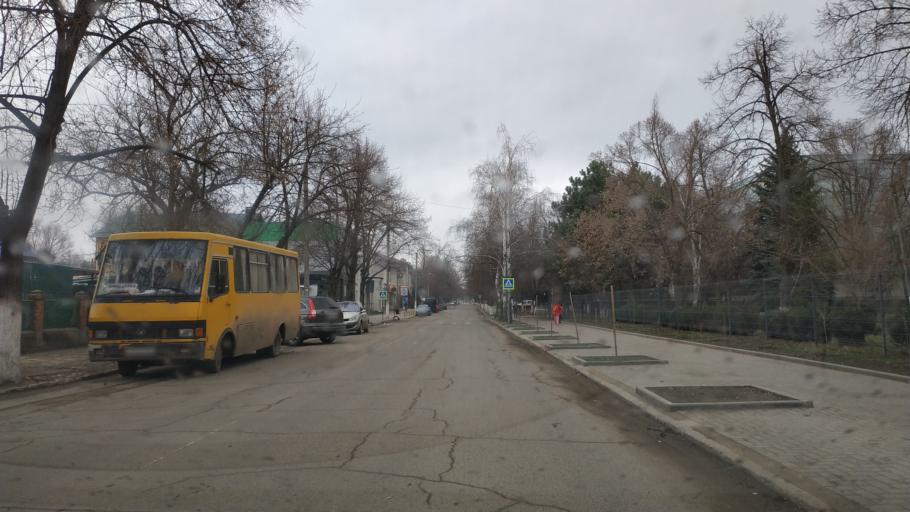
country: MD
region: Leova
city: Leova
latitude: 46.4822
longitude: 28.2516
